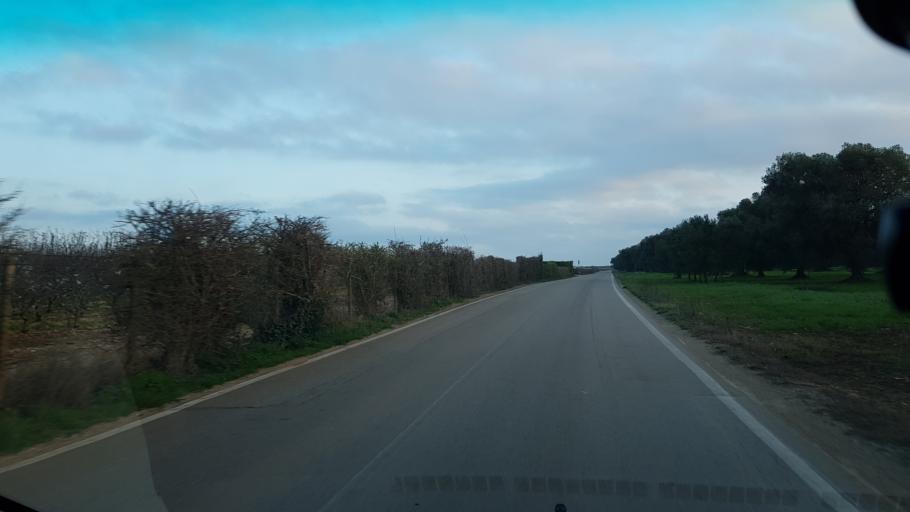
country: IT
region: Apulia
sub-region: Provincia di Brindisi
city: San Vito dei Normanni
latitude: 40.6342
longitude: 17.7818
